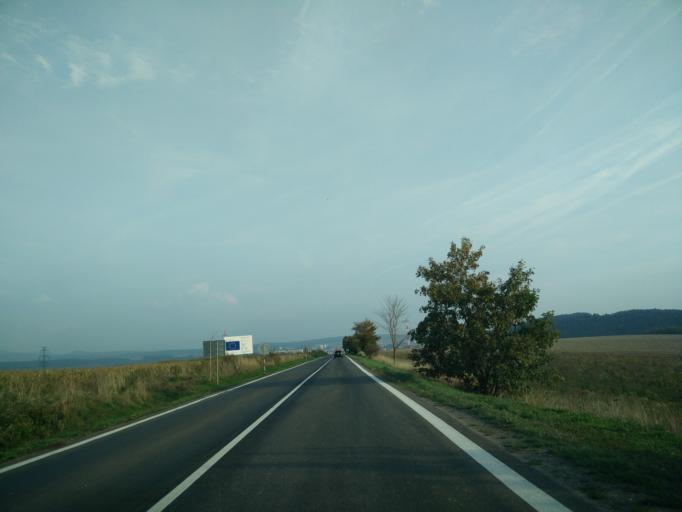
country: SK
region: Nitriansky
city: Banovce nad Bebravou
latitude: 48.7550
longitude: 18.2054
